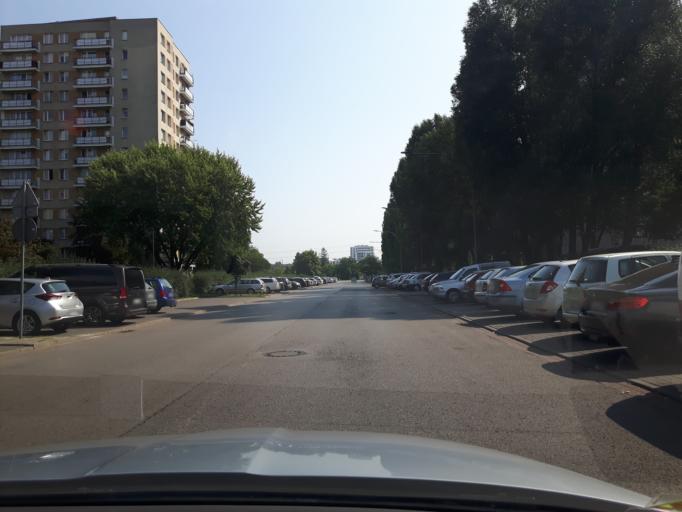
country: PL
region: Masovian Voivodeship
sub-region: Warszawa
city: Targowek
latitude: 52.2996
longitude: 21.0457
